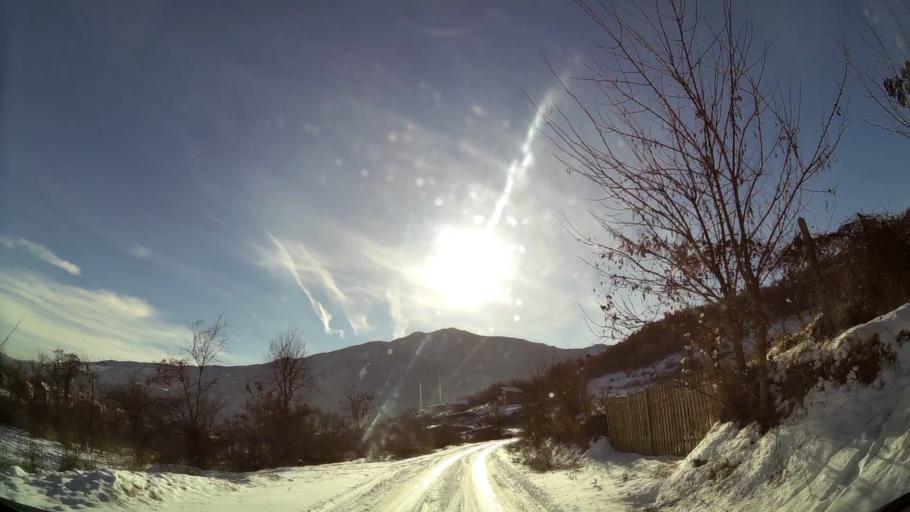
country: MK
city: Ljubin
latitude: 41.9826
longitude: 21.3001
